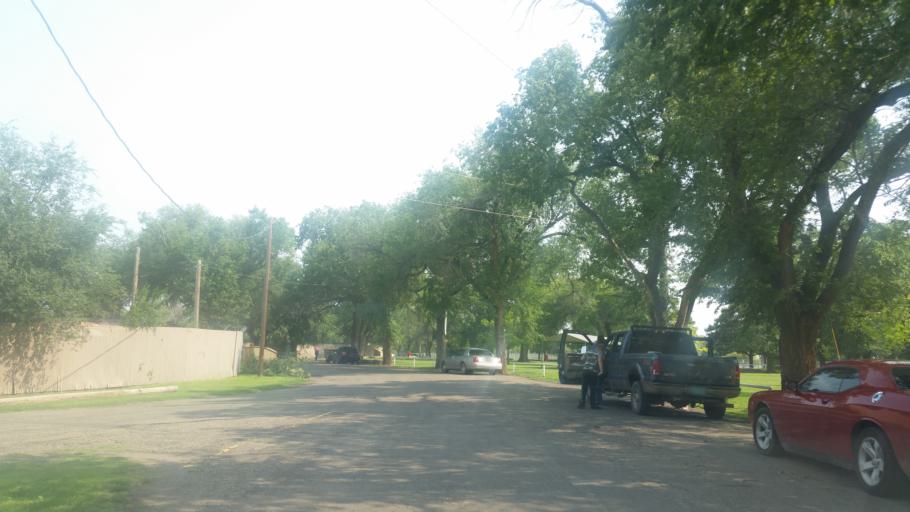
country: US
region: New Mexico
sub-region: Curry County
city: Clovis
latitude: 34.4089
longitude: -103.1859
